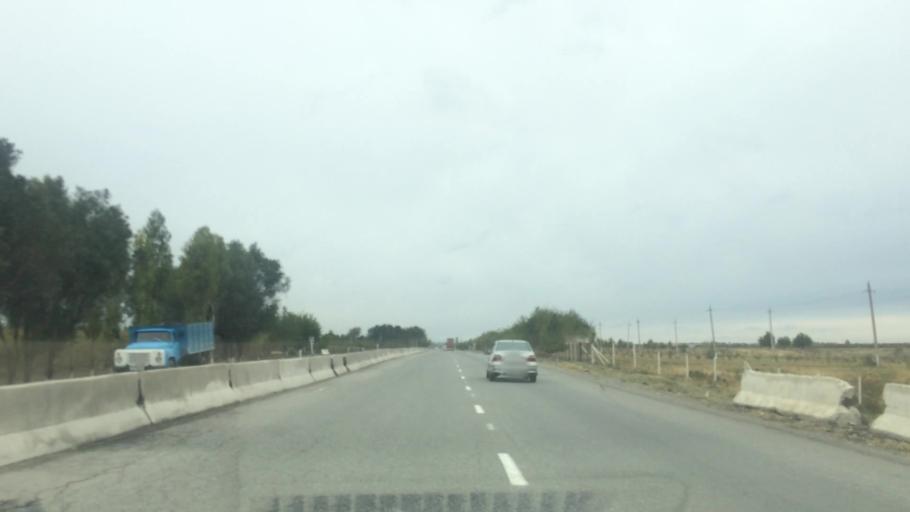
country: UZ
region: Samarqand
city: Bulung'ur
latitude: 39.7830
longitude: 67.3023
